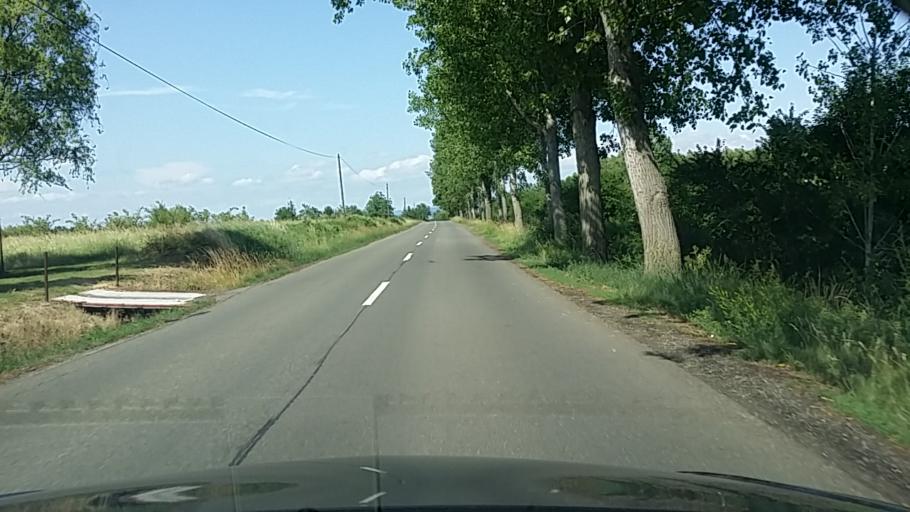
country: SK
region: Nitriansky
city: Sahy
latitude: 48.0296
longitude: 18.9007
